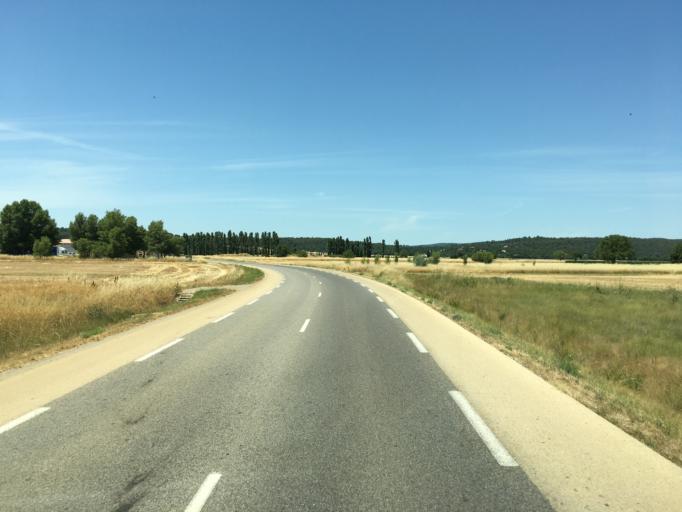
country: FR
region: Provence-Alpes-Cote d'Azur
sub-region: Departement du Var
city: Saint-Maximin-la-Sainte-Baume
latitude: 43.4595
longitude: 5.8523
